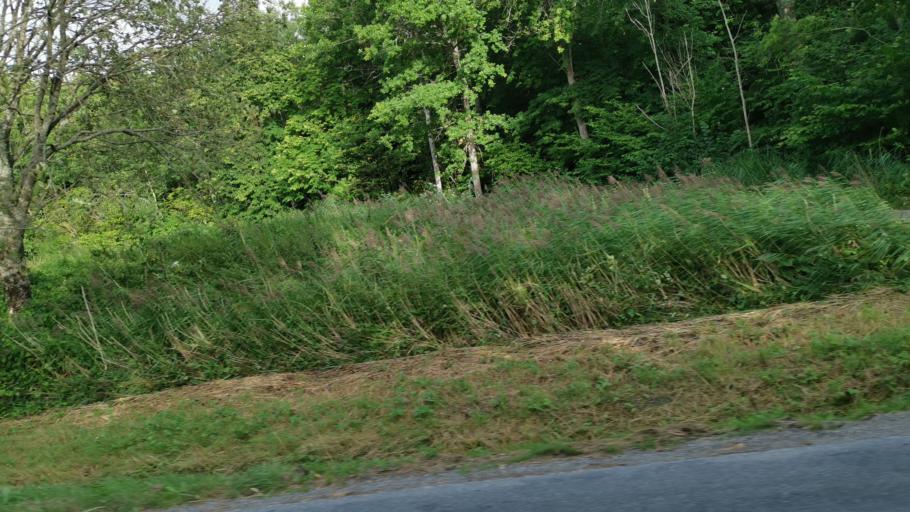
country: SE
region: Vaestra Goetaland
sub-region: Sotenas Kommun
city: Hunnebostrand
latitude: 58.5108
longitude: 11.3155
